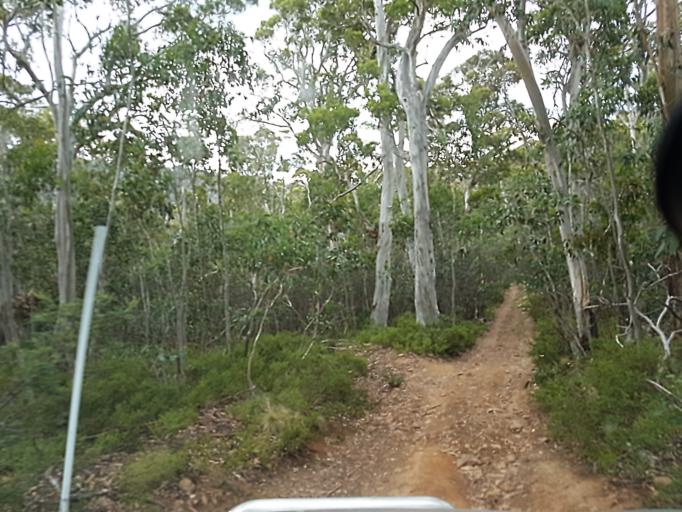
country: AU
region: New South Wales
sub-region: Snowy River
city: Jindabyne
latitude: -36.8765
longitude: 148.1619
